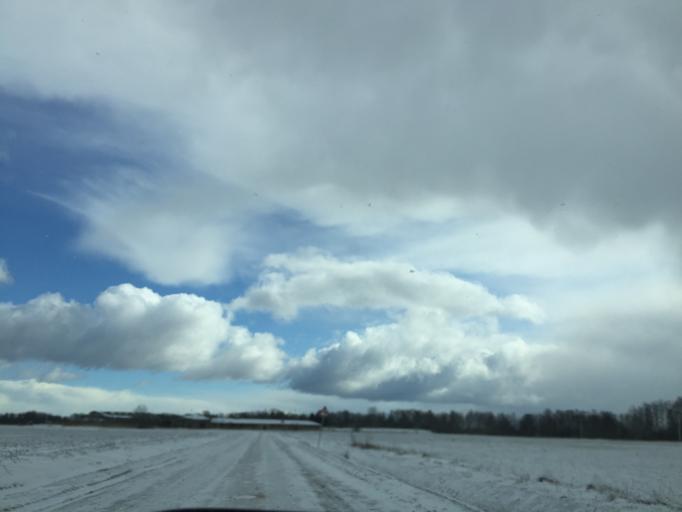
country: LV
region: Ventspils
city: Ventspils
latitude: 57.3720
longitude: 21.6263
